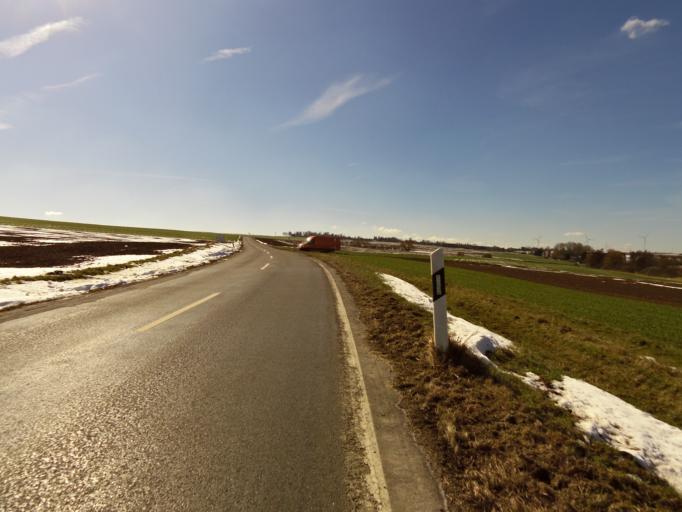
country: DE
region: Rheinland-Pfalz
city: Ottersheim
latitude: 49.6199
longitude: 8.1142
